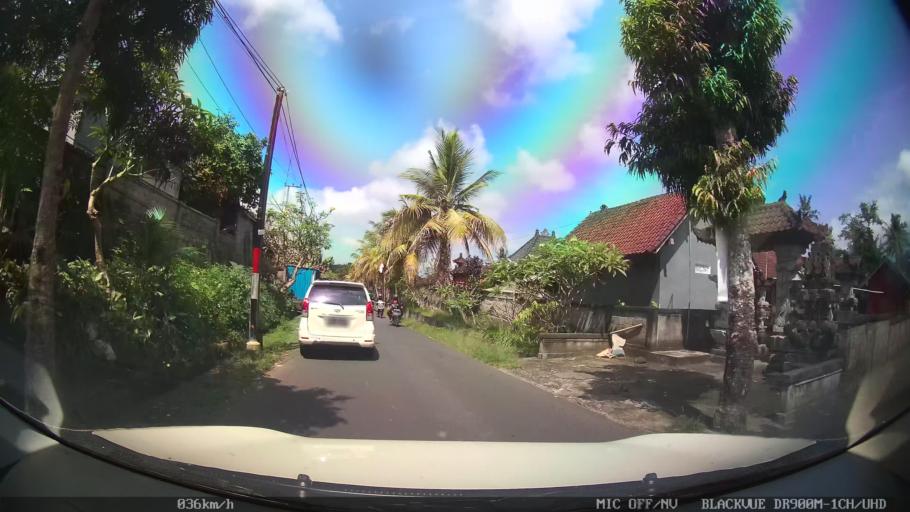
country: ID
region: Bali
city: Banjar Mulung
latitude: -8.5139
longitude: 115.3190
